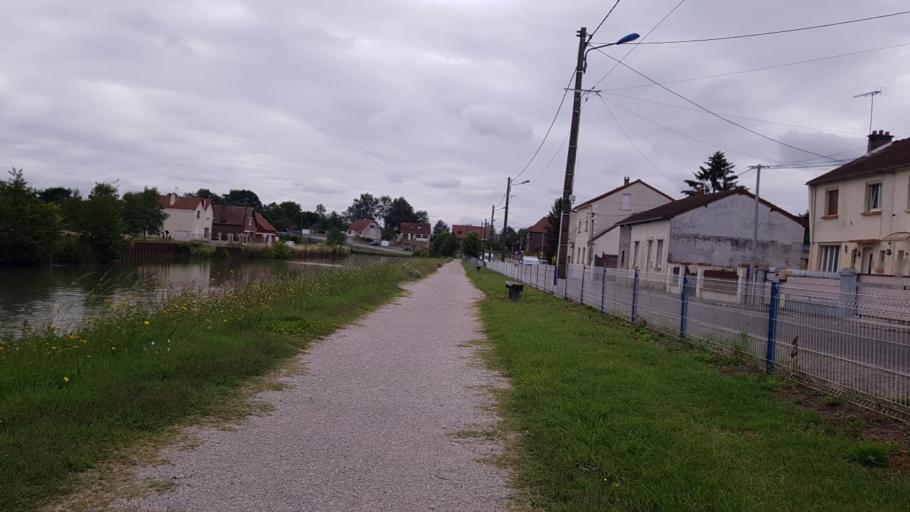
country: FR
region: Picardie
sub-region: Departement de l'Aisne
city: Beautor
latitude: 49.6545
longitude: 3.3439
